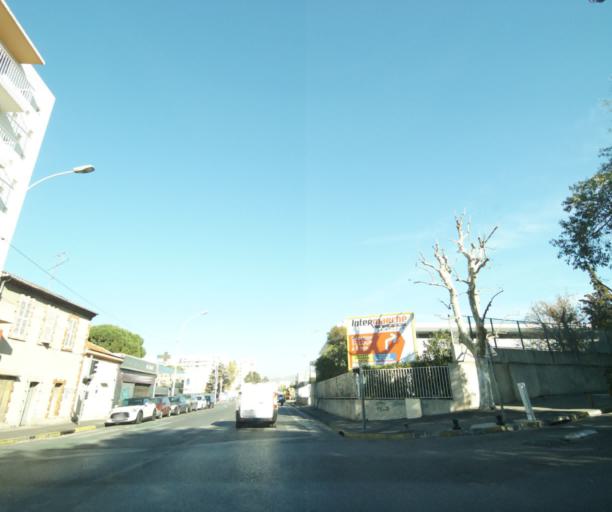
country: FR
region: Provence-Alpes-Cote d'Azur
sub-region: Departement des Bouches-du-Rhone
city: Marseille 10
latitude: 43.2774
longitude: 5.4203
